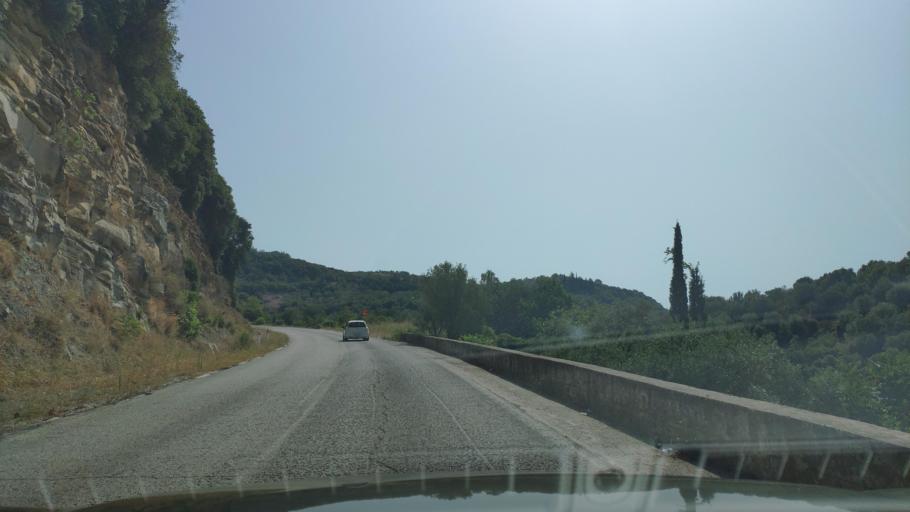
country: GR
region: Epirus
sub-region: Nomos Artas
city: Peta
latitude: 39.1610
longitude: 21.0341
